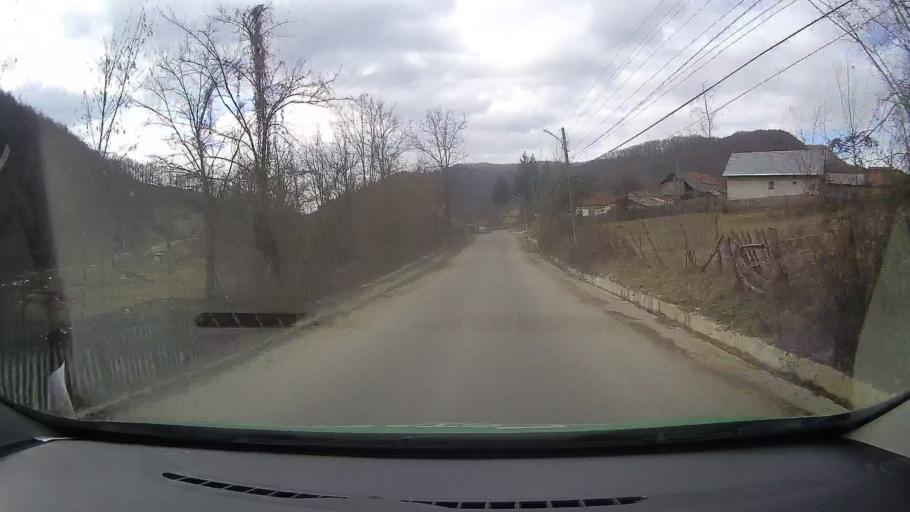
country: RO
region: Dambovita
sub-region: Comuna Visinesti
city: Visinesti
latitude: 45.0995
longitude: 25.5789
